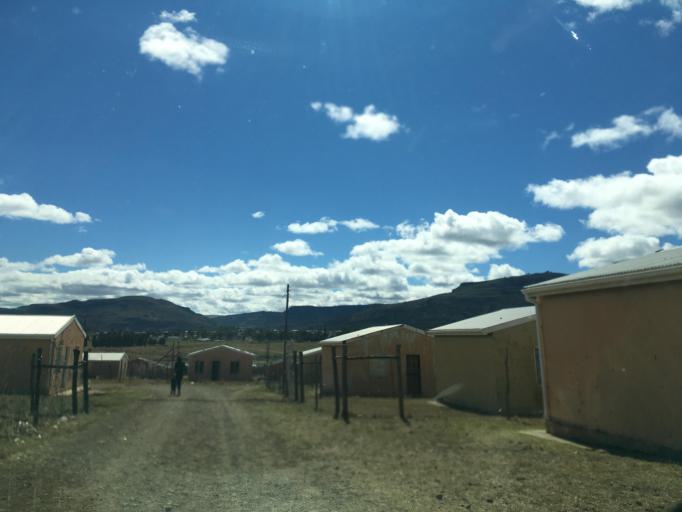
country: ZA
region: Eastern Cape
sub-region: Chris Hani District Municipality
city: Cala
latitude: -31.5408
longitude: 27.6819
